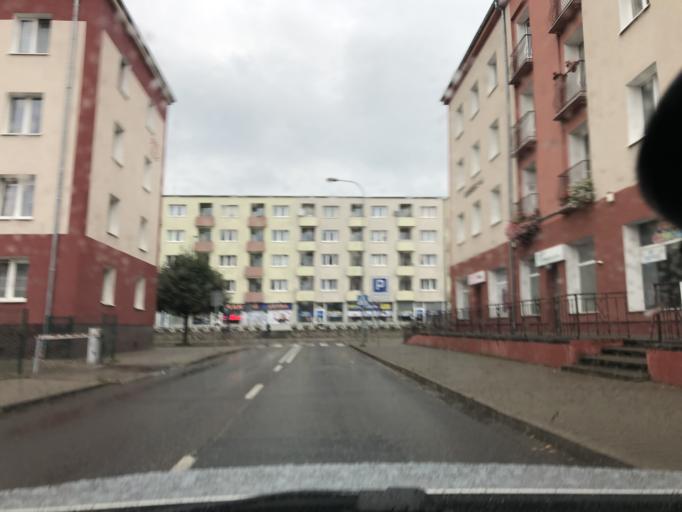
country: PL
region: Greater Poland Voivodeship
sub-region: Powiat pilski
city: Pila
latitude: 53.1499
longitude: 16.7331
